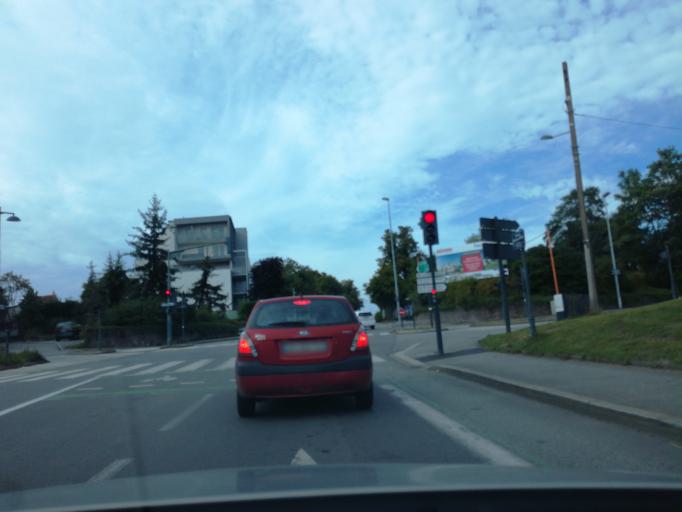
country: FR
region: Brittany
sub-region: Departement d'Ille-et-Vilaine
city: Rennes
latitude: 48.1383
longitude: -1.6586
